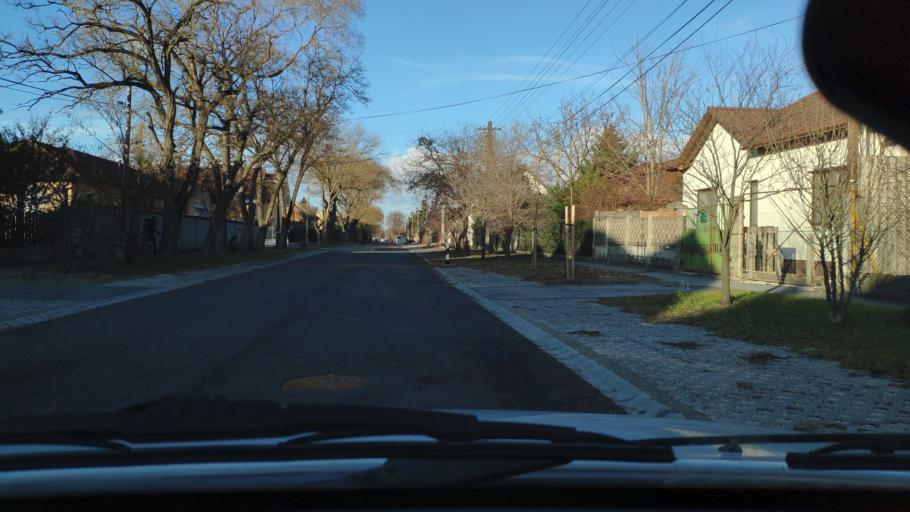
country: HU
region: Budapest
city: Budapest XXI. keruelet
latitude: 47.4193
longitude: 19.0807
